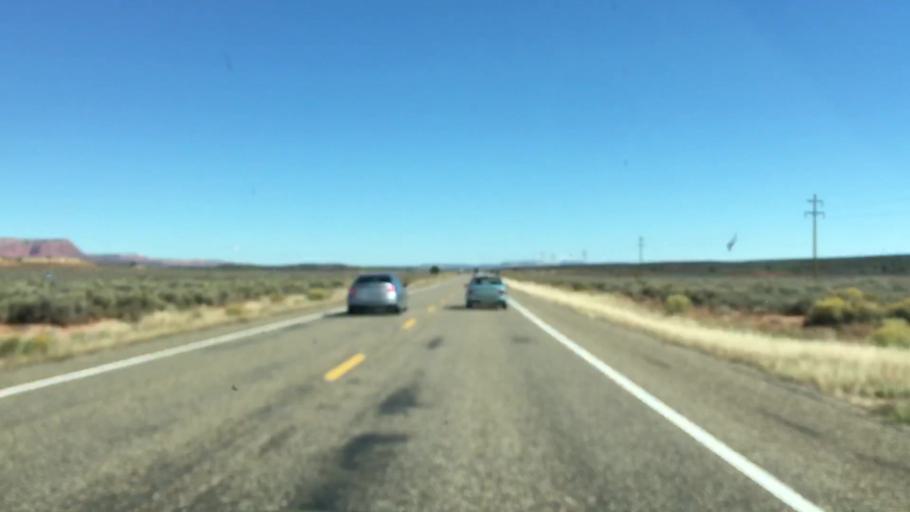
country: US
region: Utah
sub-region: Kane County
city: Kanab
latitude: 37.1169
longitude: -112.1091
